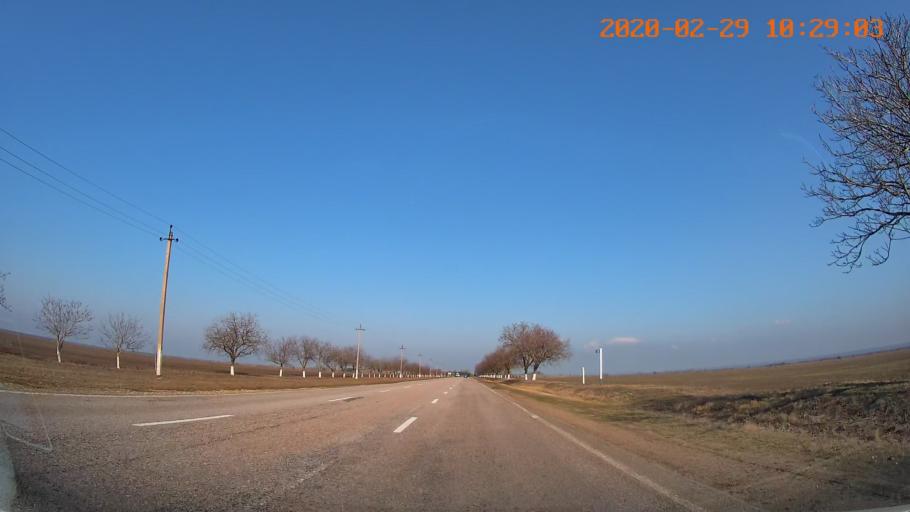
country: MD
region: Telenesti
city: Tiraspolul Nou
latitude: 46.9187
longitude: 29.5879
